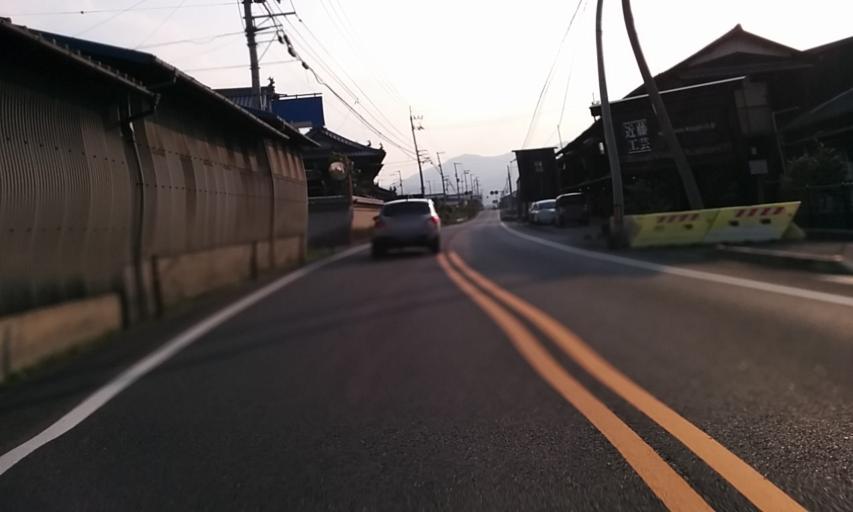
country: JP
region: Ehime
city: Saijo
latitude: 33.8721
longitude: 133.0581
